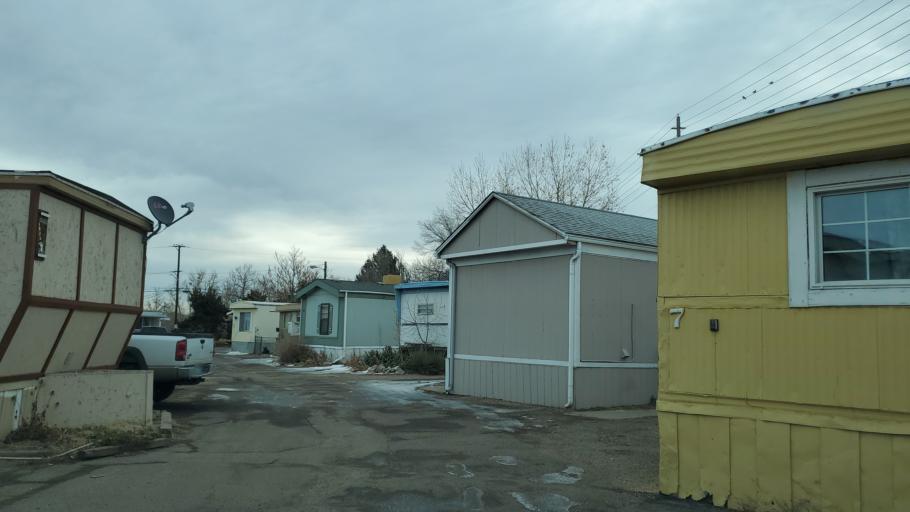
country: US
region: Colorado
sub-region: Denver County
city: Denver
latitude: 39.6988
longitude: -104.9977
